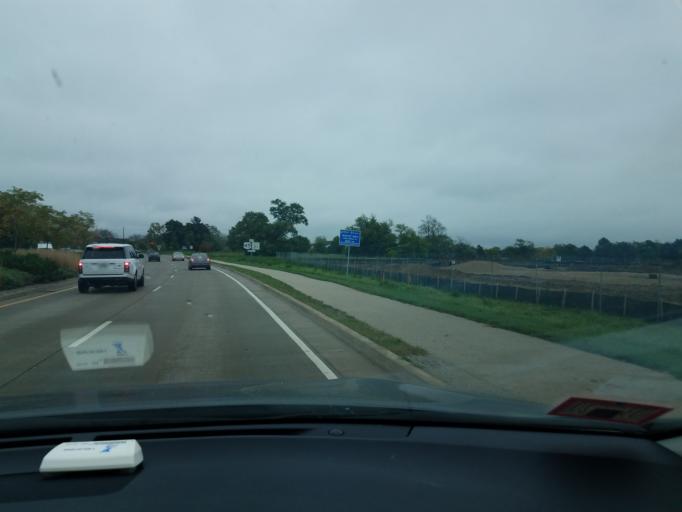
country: US
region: Illinois
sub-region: Lake County
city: Lincolnshire
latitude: 42.1973
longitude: -87.9347
